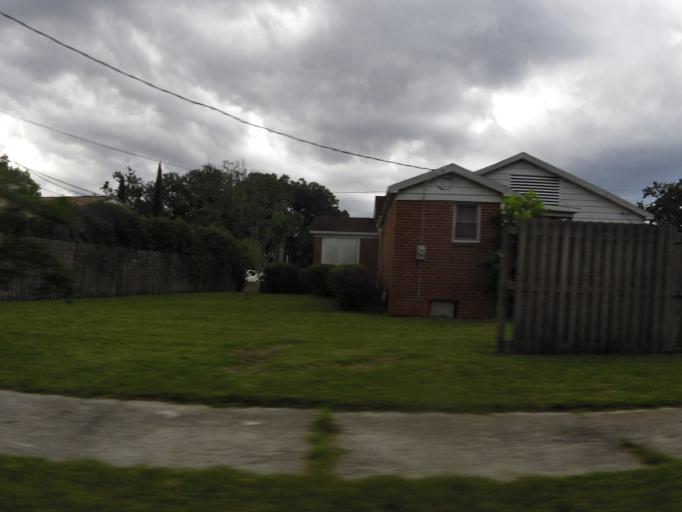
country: US
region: Florida
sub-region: Duval County
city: Jacksonville
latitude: 30.3055
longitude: -81.6392
